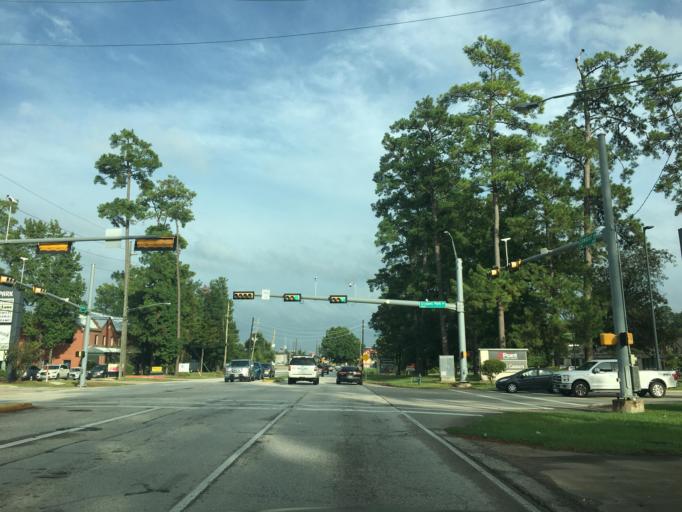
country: US
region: Texas
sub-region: Montgomery County
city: Oak Ridge North
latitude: 30.1265
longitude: -95.4578
